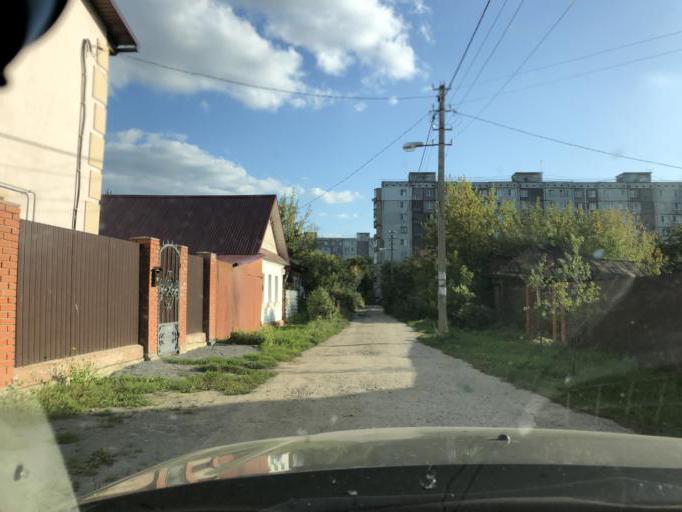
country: RU
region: Tula
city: Tula
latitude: 54.2118
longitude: 37.6065
